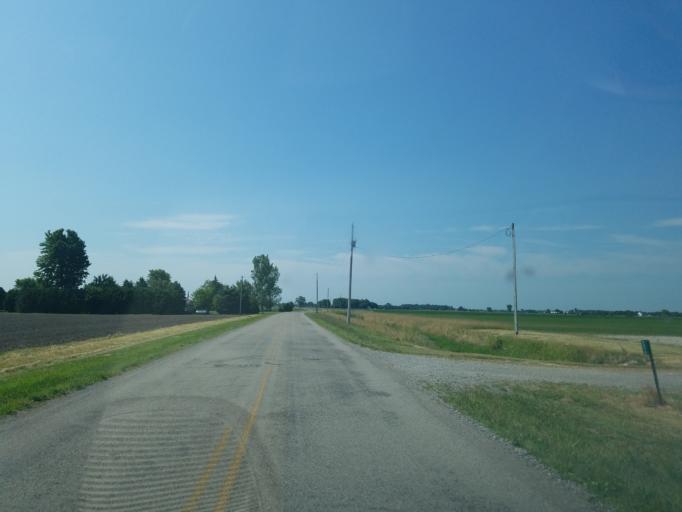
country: US
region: Ohio
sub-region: Van Wert County
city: Van Wert
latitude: 40.9043
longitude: -84.6294
